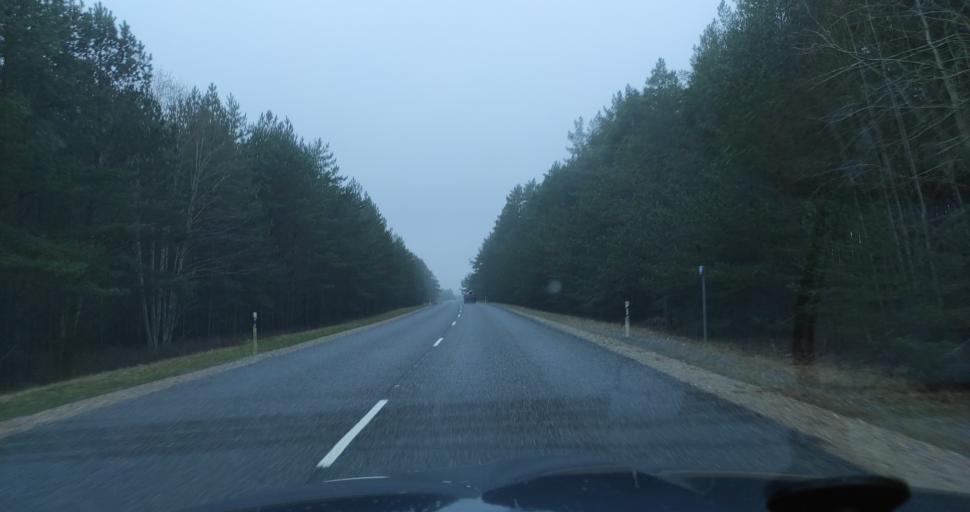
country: LV
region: Pavilostas
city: Pavilosta
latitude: 56.9685
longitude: 21.3418
